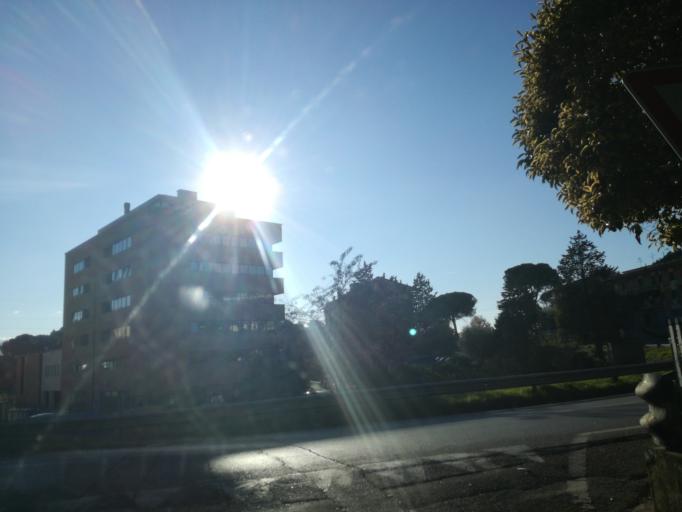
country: IT
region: Umbria
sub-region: Provincia di Perugia
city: Perugia
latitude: 43.0769
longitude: 12.4011
